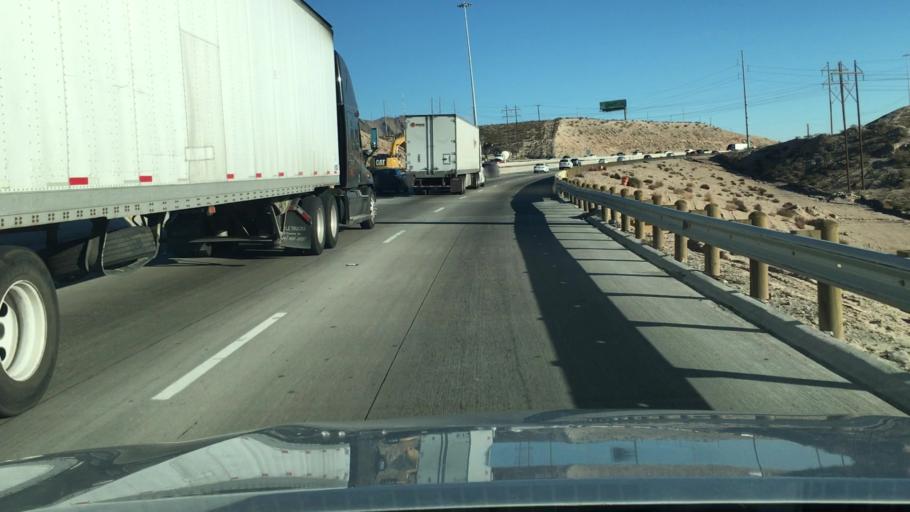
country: US
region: New Mexico
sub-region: Dona Ana County
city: Sunland Park
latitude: 31.8087
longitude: -106.5261
